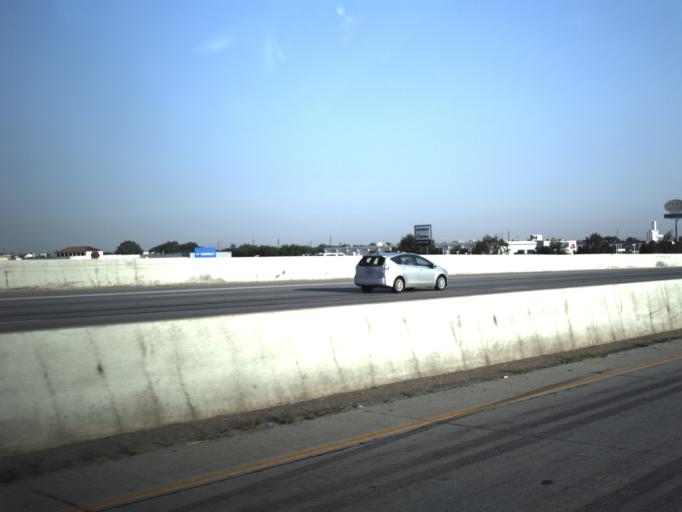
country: US
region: Utah
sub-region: Salt Lake County
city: South Salt Lake
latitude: 40.7359
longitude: -111.9042
